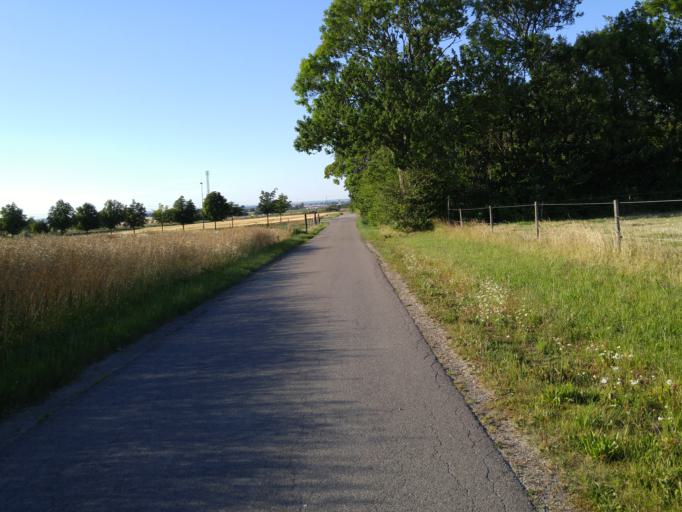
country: SE
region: Skane
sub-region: Lunds Kommun
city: Lund
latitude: 55.7361
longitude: 13.1930
